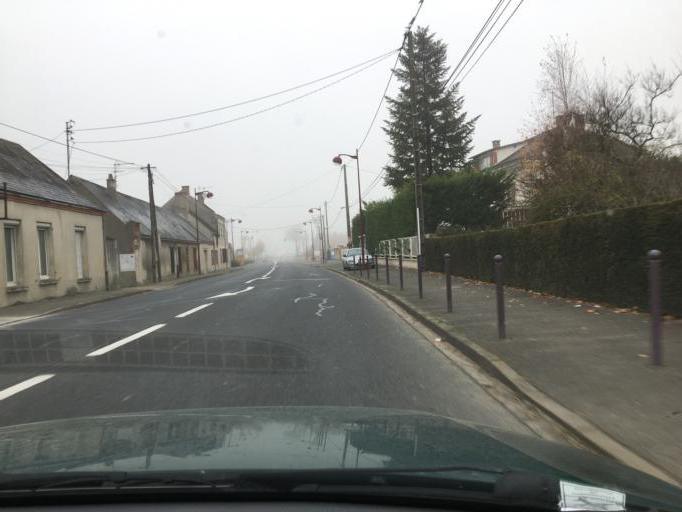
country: FR
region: Centre
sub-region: Departement du Loiret
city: Saran
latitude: 47.9876
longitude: 1.8827
